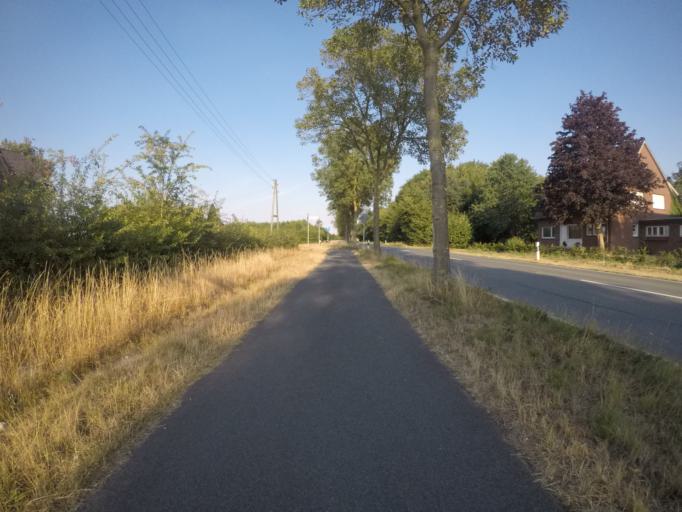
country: DE
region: North Rhine-Westphalia
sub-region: Regierungsbezirk Dusseldorf
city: Bocholt
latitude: 51.8474
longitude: 6.5784
